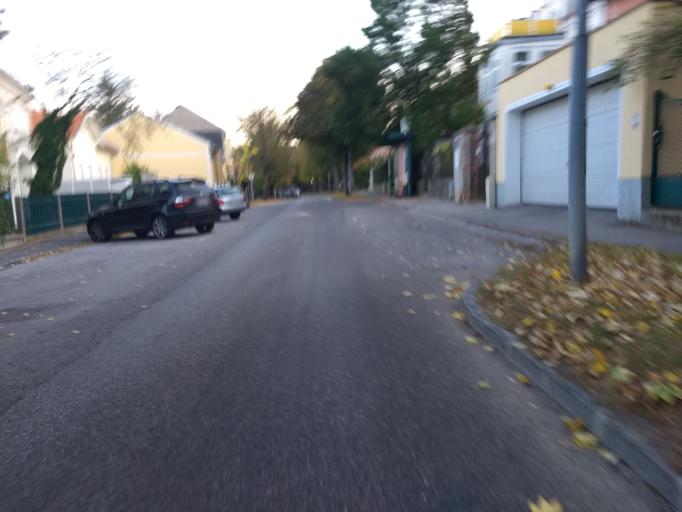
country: AT
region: Lower Austria
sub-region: Politischer Bezirk Modling
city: Perchtoldsdorf
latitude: 48.1250
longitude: 16.2580
